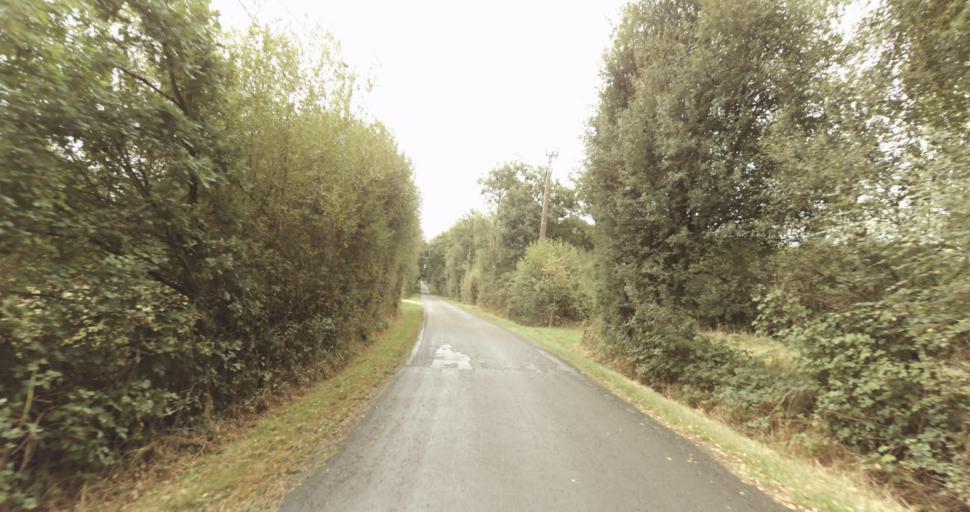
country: FR
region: Lower Normandy
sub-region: Departement de l'Orne
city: Sainte-Gauburge-Sainte-Colombe
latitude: 48.6981
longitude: 0.4542
